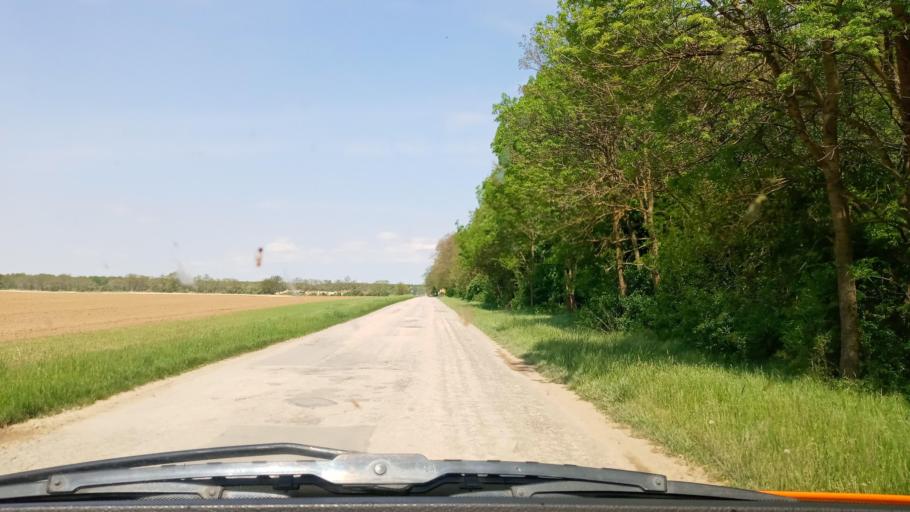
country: HU
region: Baranya
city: Boly
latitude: 45.8836
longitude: 18.5697
